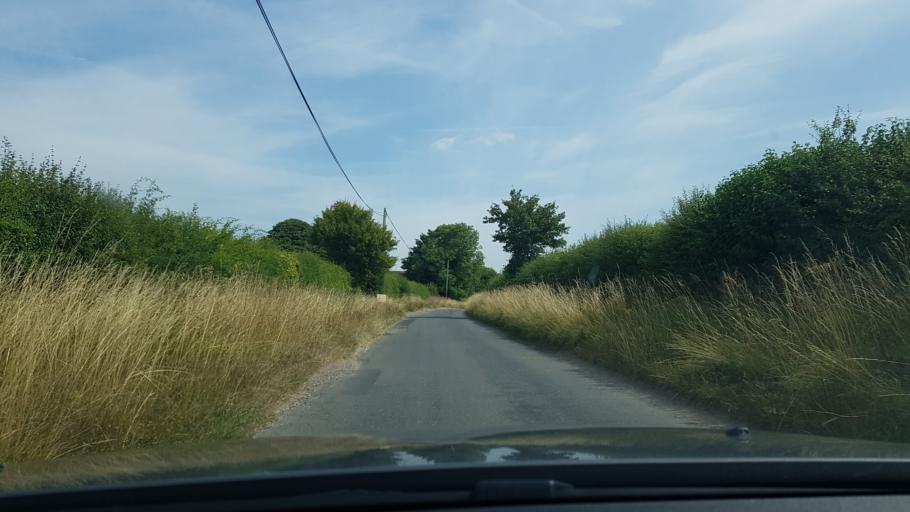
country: GB
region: England
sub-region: West Berkshire
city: Lambourn
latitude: 51.5139
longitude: -1.5171
